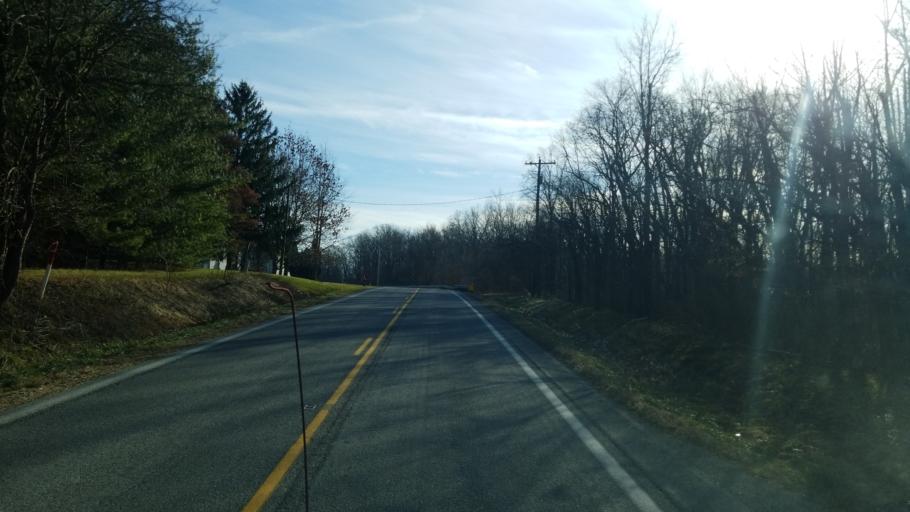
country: US
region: Ohio
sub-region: Sandusky County
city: Green Springs
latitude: 41.2970
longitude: -83.0518
